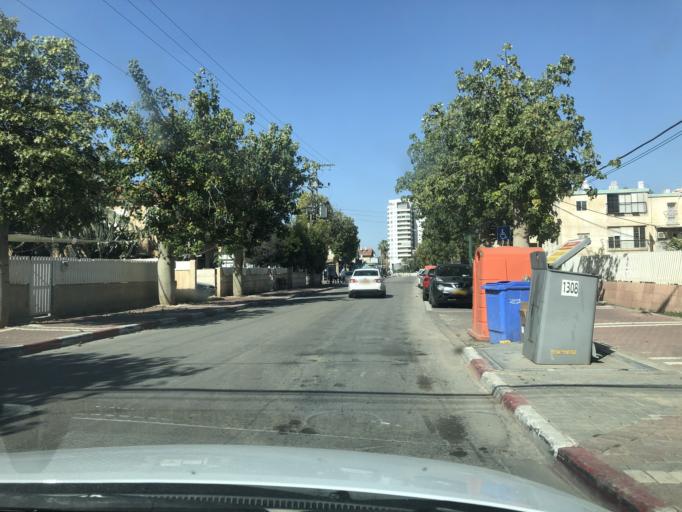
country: IL
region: Southern District
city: Beersheba
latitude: 31.2559
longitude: 34.7952
